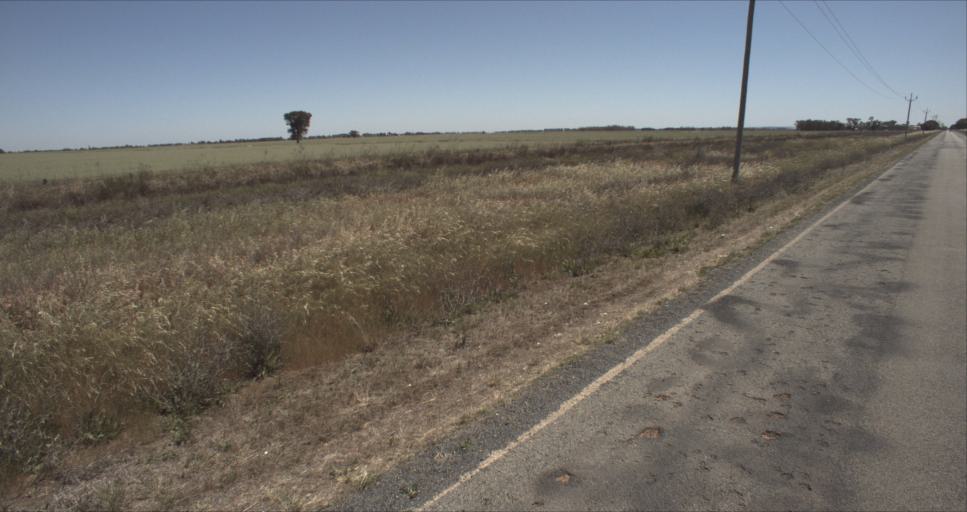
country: AU
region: New South Wales
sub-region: Leeton
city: Leeton
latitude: -34.5097
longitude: 146.2853
